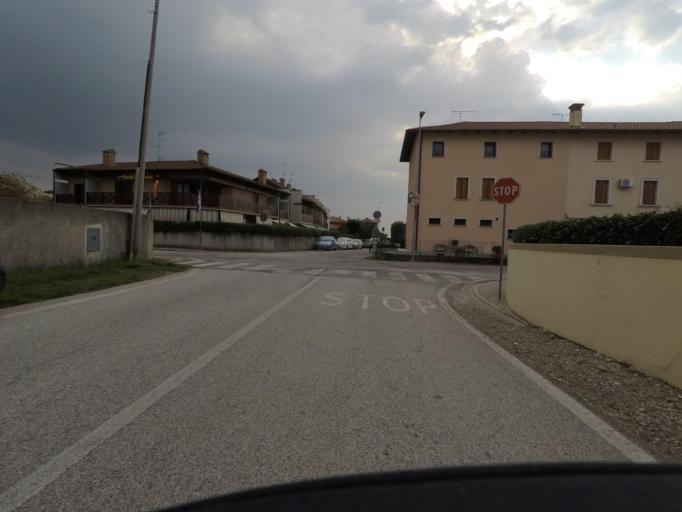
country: IT
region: Friuli Venezia Giulia
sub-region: Provincia di Udine
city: Tavagnacco
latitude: 46.1109
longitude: 13.2398
